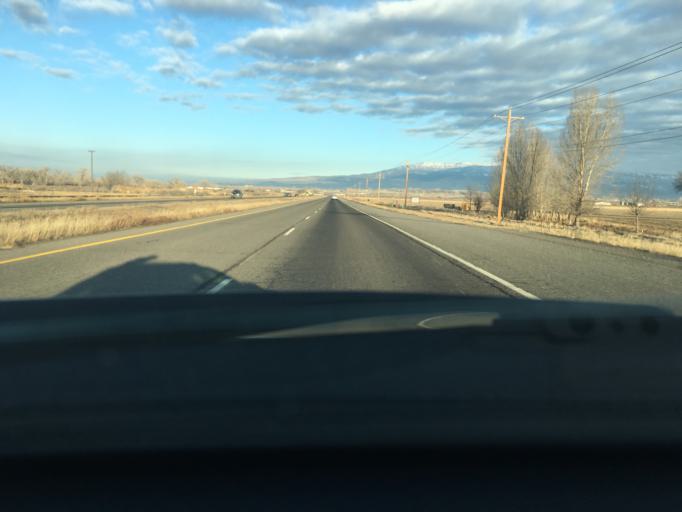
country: US
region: Colorado
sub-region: Delta County
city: Delta
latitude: 38.6883
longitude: -108.0130
